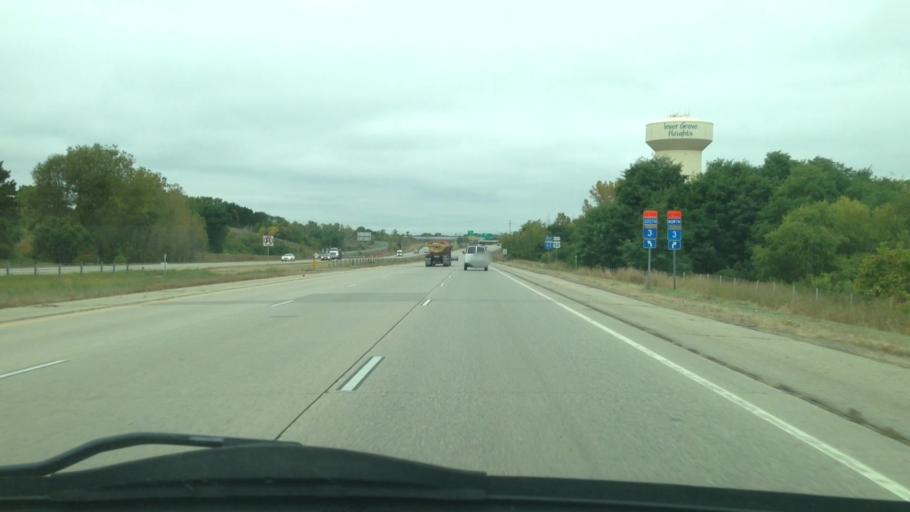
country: US
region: Minnesota
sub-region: Dakota County
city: Inver Grove Heights
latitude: 44.8182
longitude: -93.0483
